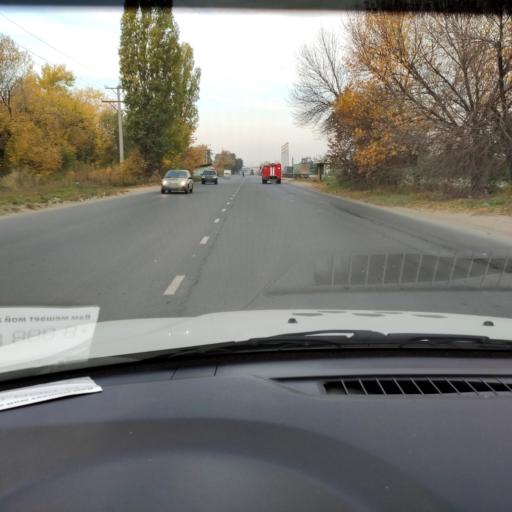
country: RU
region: Samara
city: Tol'yatti
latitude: 53.5323
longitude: 49.4550
